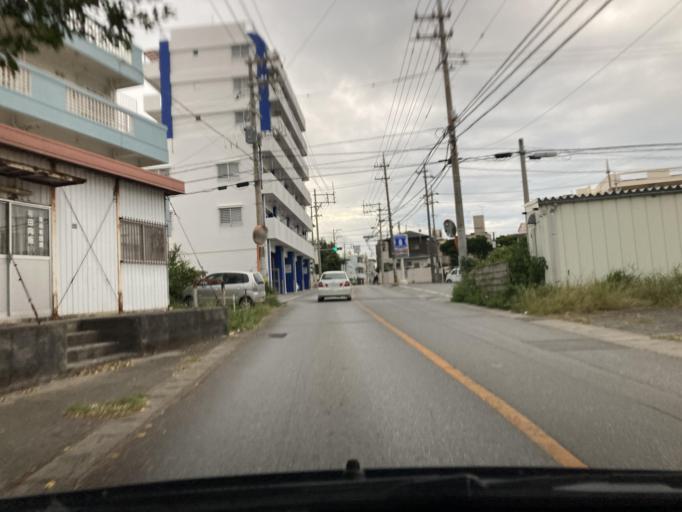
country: JP
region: Okinawa
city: Ginowan
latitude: 26.2739
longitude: 127.7415
